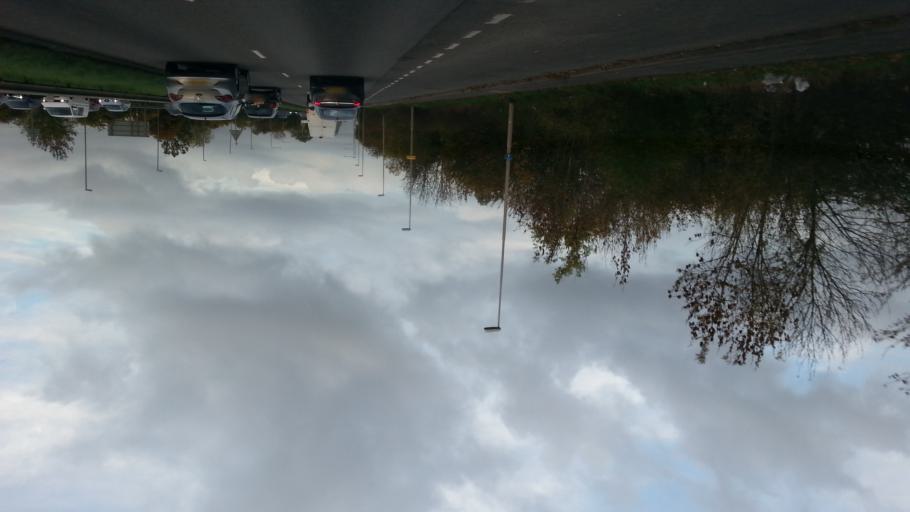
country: GB
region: England
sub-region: Derbyshire
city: Pinxton
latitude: 53.1117
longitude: -1.2960
